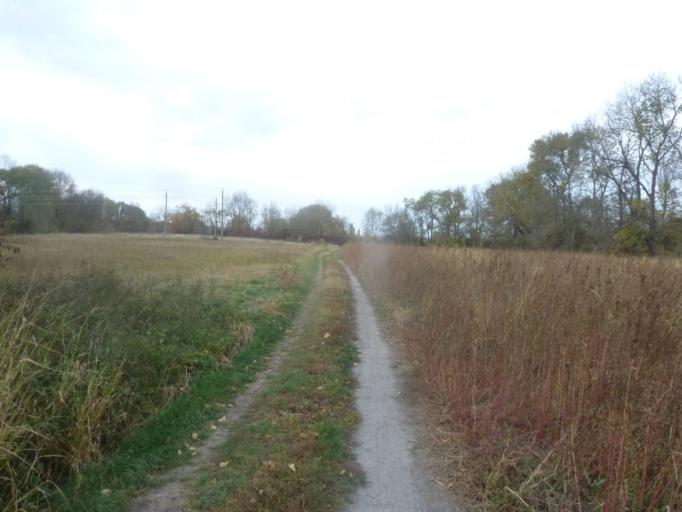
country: HU
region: Pest
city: Ocsa
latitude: 47.2809
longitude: 19.2321
